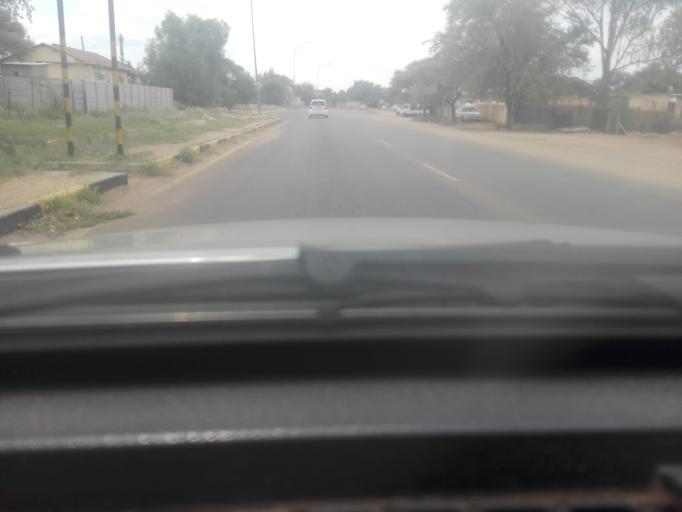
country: BW
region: South East
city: Gaborone
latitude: -24.6231
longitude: 25.9434
